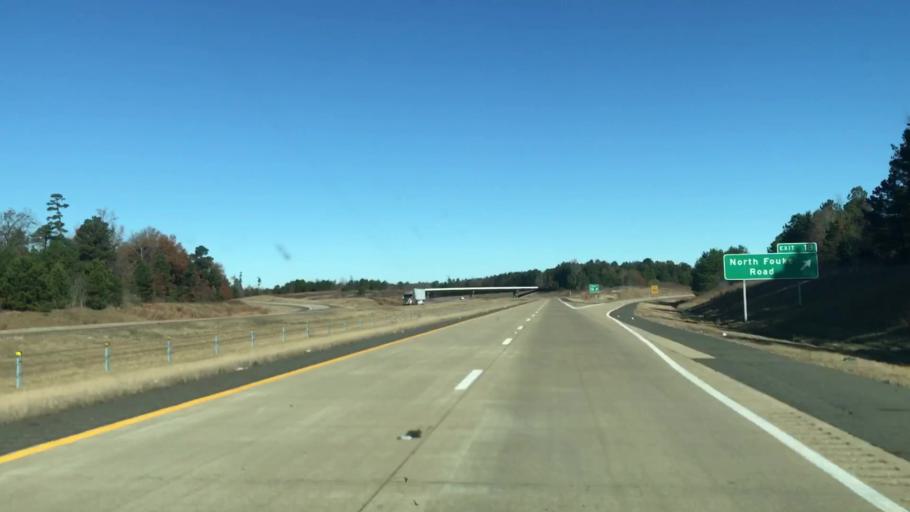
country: US
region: Texas
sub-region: Bowie County
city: Texarkana
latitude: 33.2639
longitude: -93.8974
